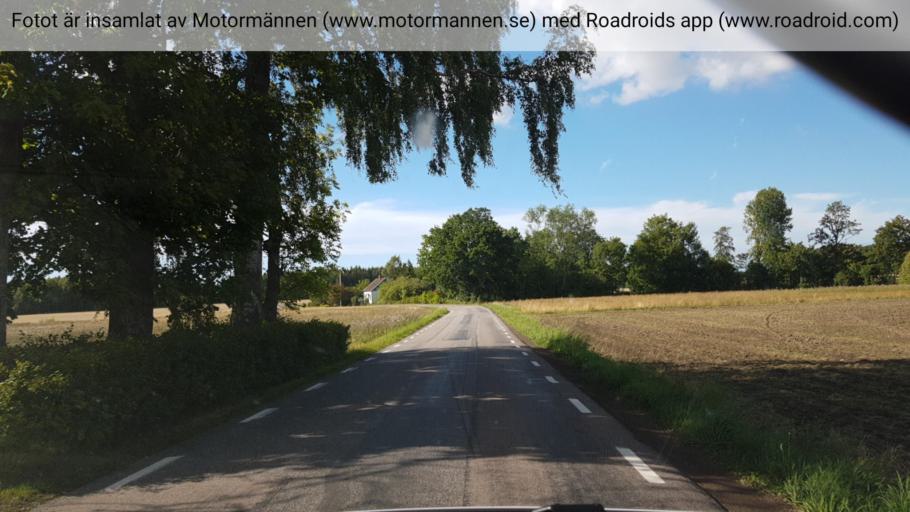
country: SE
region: Vaestra Goetaland
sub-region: Gotene Kommun
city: Kallby
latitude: 58.4794
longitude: 13.3197
